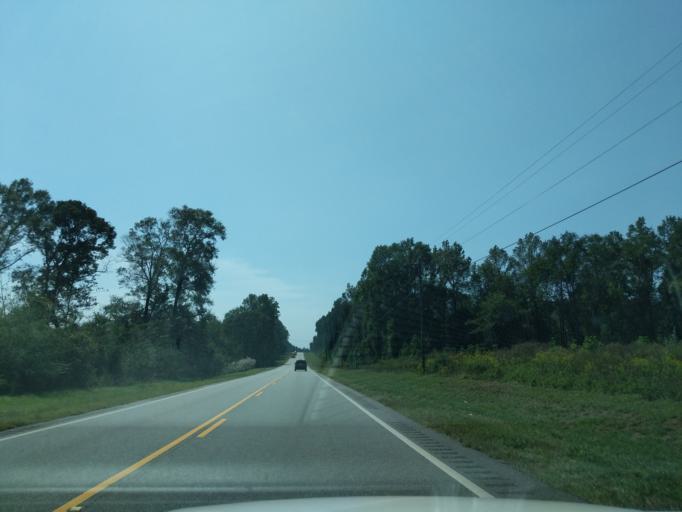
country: US
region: Alabama
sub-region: Covington County
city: Andalusia
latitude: 31.2232
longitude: -86.5305
